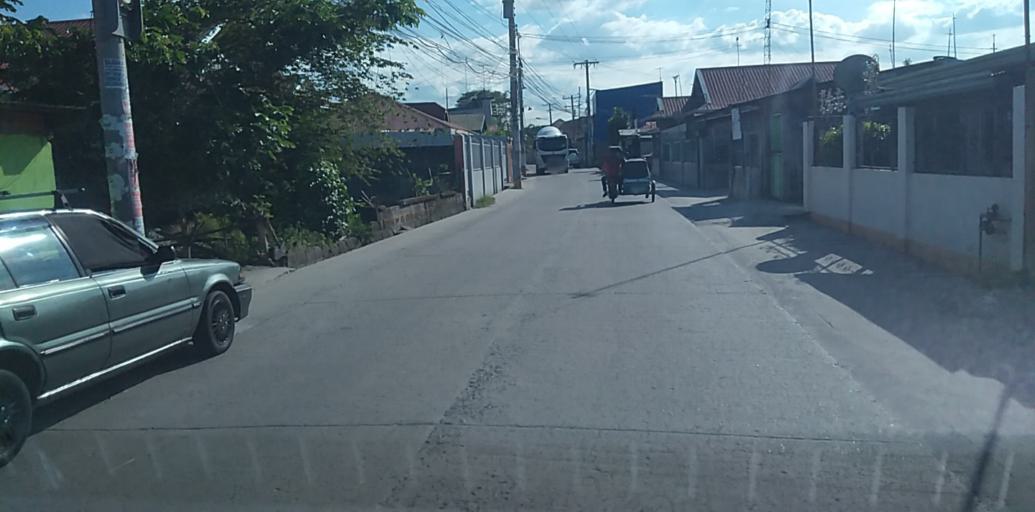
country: PH
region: Central Luzon
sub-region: Province of Pampanga
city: Acli
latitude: 15.1144
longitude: 120.6335
